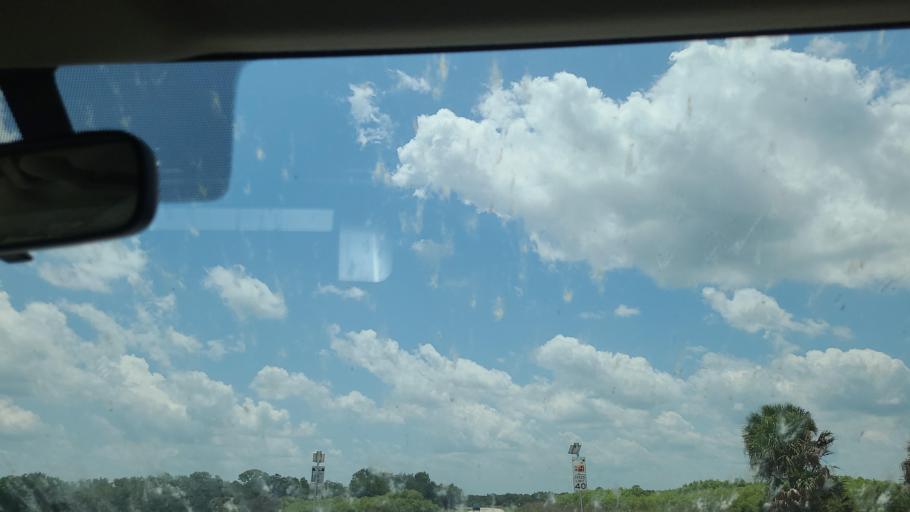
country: US
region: Florida
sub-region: Glades County
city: Buckhead Ridge
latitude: 27.1036
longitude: -81.0696
